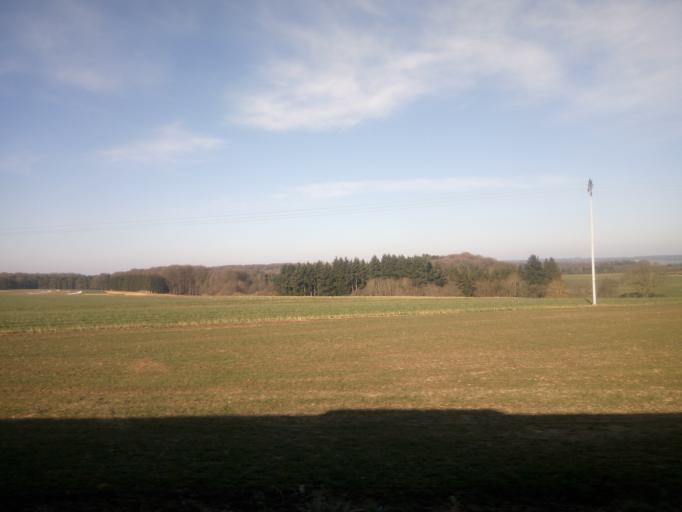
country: LU
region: Grevenmacher
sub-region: Canton d'Echternach
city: Consdorf
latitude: 49.7654
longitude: 6.3382
